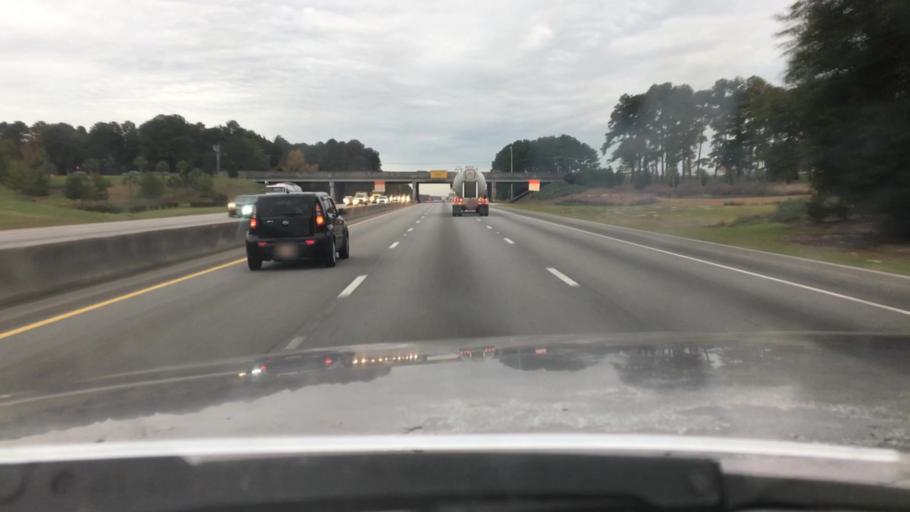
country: US
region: South Carolina
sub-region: Lexington County
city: Oak Grove
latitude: 34.0123
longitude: -81.1466
